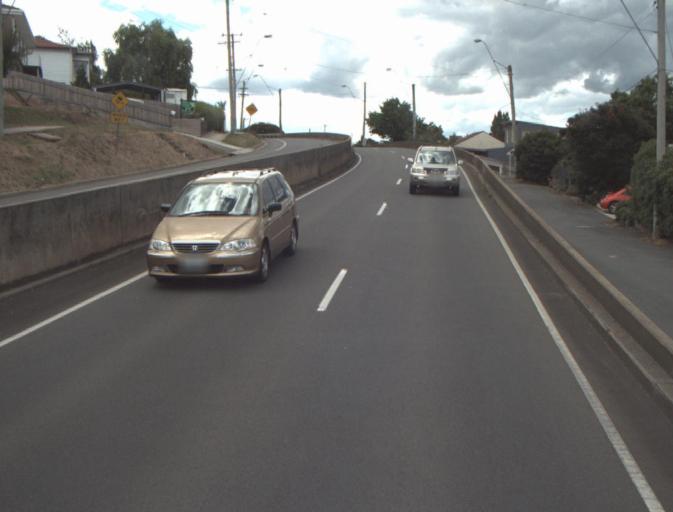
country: AU
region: Tasmania
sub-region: Launceston
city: Launceston
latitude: -41.4267
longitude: 147.1173
